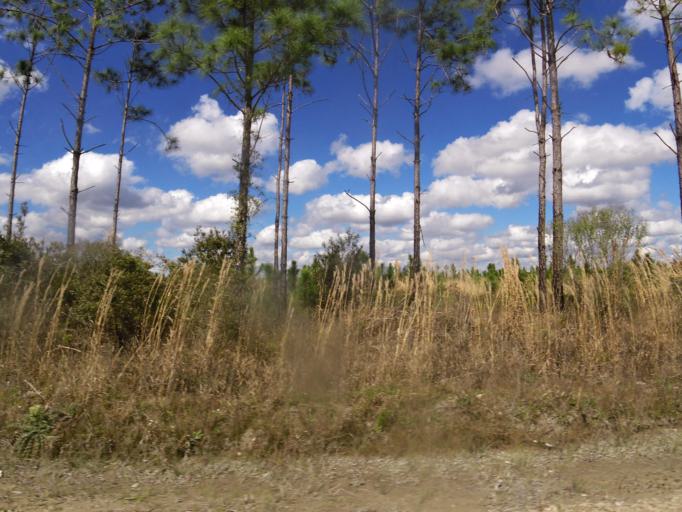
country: US
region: Florida
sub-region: Clay County
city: Green Cove Springs
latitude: 29.8473
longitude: -81.7232
